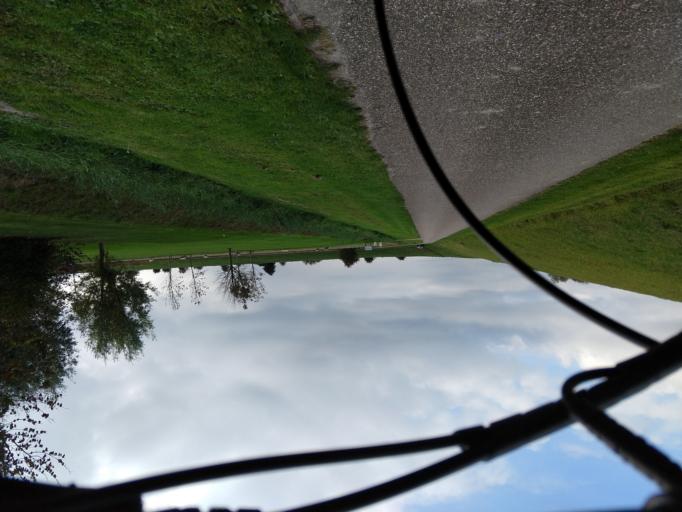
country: NL
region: South Holland
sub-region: Gemeente Goeree-Overflakkee
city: Goedereede
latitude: 51.7173
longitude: 3.9764
